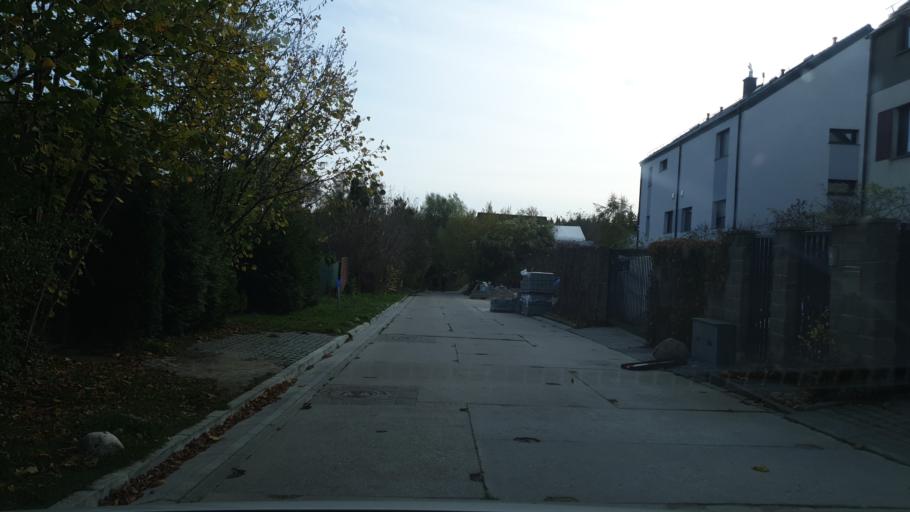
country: PL
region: Pomeranian Voivodeship
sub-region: Powiat gdanski
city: Kowale
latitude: 54.3482
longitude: 18.5917
